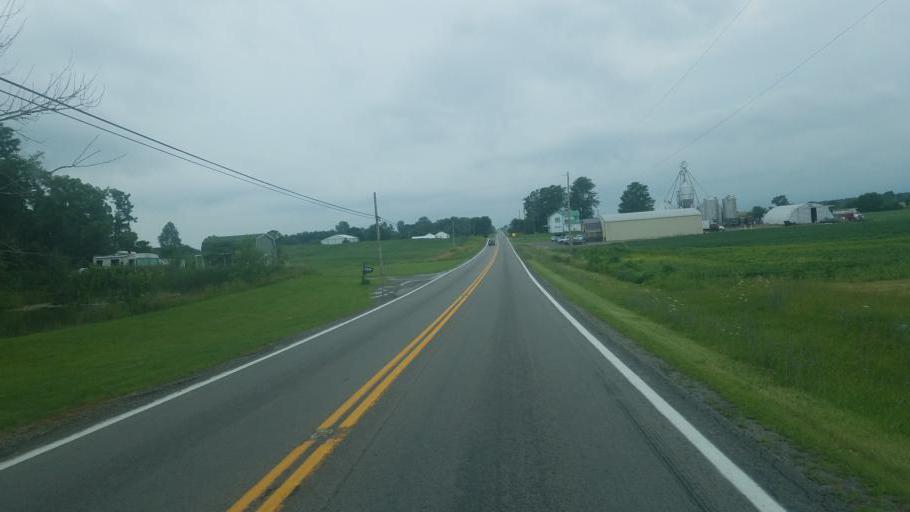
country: US
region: Ohio
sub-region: Hardin County
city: Kenton
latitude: 40.6061
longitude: -83.7067
